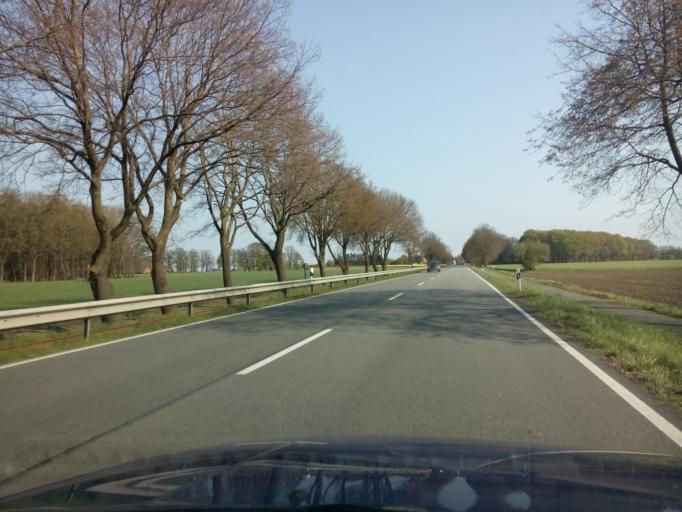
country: DE
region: Lower Saxony
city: Asendorf
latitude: 52.7849
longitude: 8.9938
